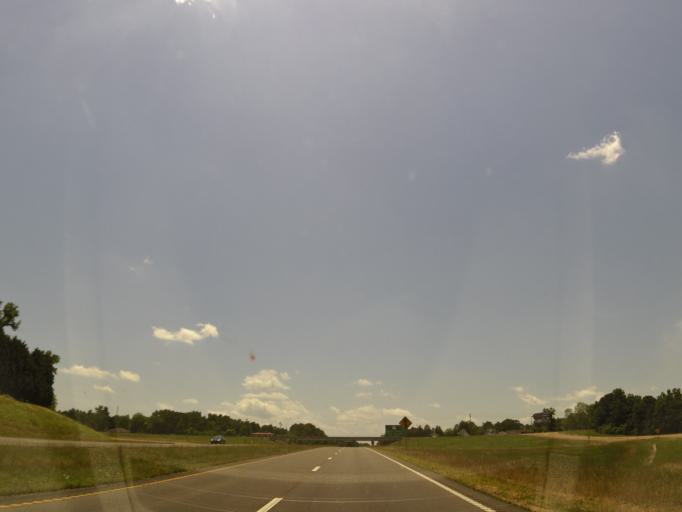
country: US
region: Mississippi
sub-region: Lafayette County
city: Oxford
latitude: 34.3568
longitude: -89.4945
